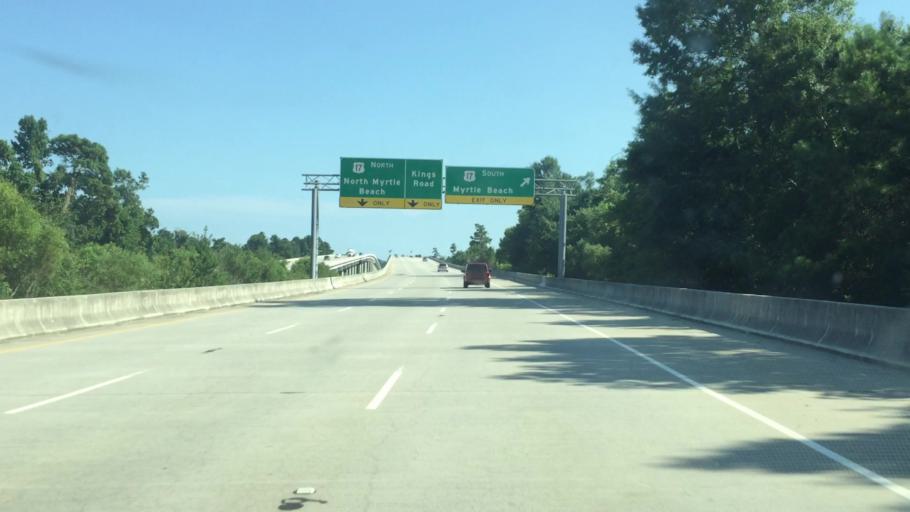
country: US
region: South Carolina
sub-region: Horry County
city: North Myrtle Beach
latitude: 33.7958
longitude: -78.7792
